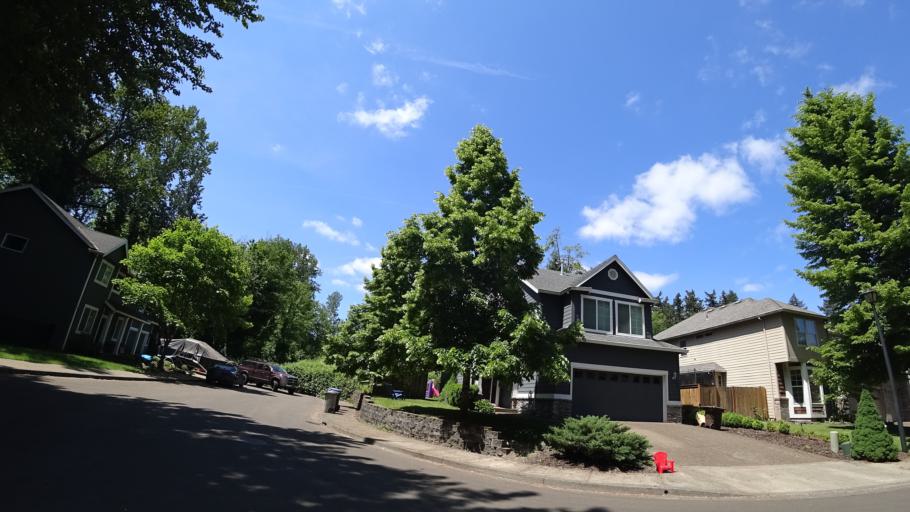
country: US
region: Oregon
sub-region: Washington County
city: Tigard
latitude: 45.4272
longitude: -122.7964
